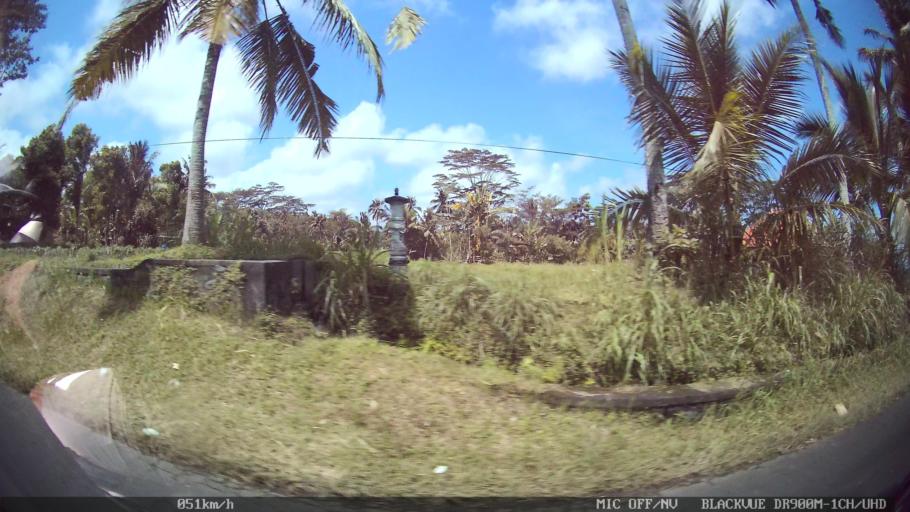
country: ID
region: Bali
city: Banjar Kelodan
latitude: -8.5084
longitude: 115.3372
